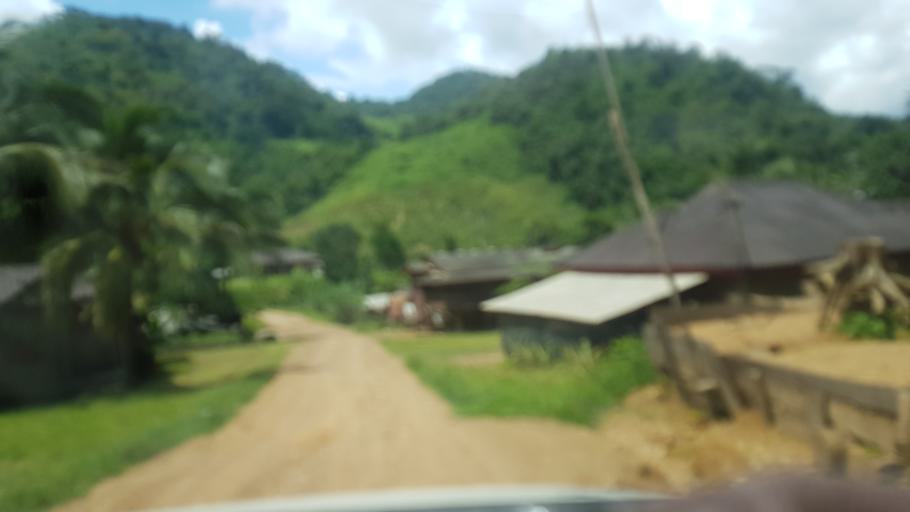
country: LA
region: Xiangkhoang
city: Phonsavan
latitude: 19.7388
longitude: 103.0778
